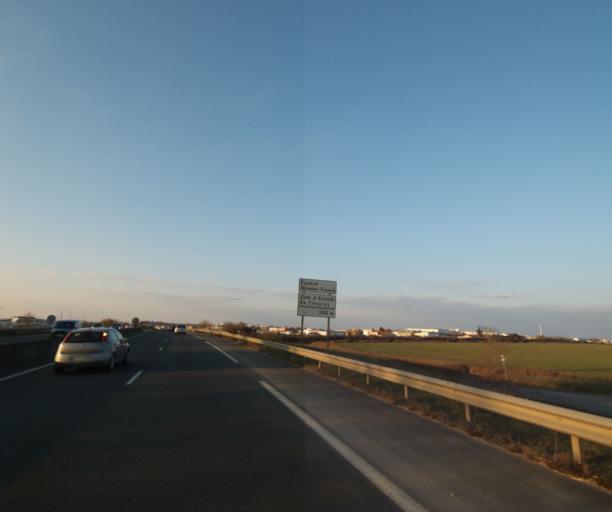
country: FR
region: Poitou-Charentes
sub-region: Departement des Deux-Sevres
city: Aiffres
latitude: 46.3266
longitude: -0.4133
